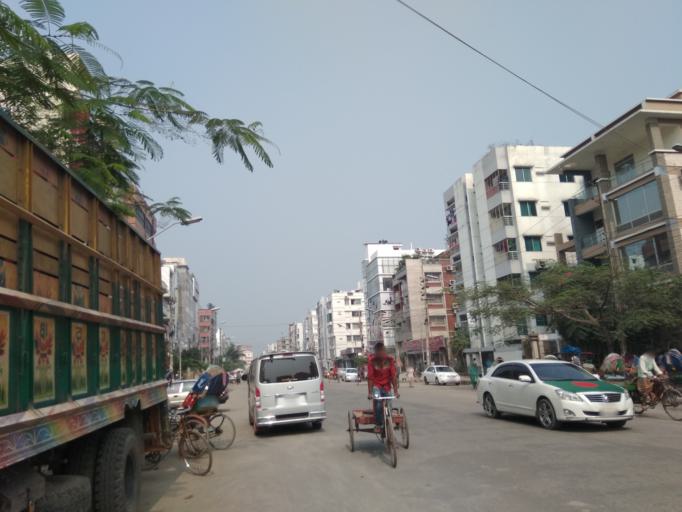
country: BD
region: Dhaka
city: Tungi
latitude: 23.8698
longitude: 90.3839
